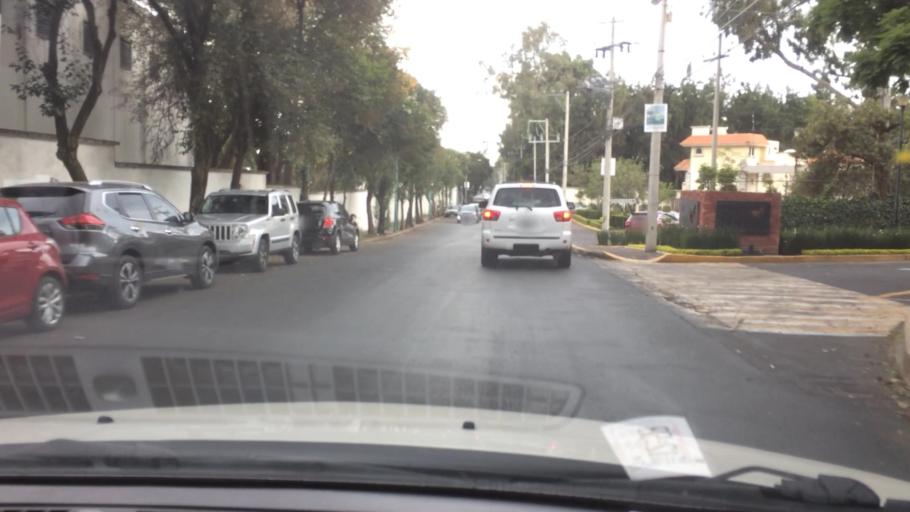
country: MX
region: Mexico City
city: Tlalpan
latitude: 19.2835
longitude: -99.1486
